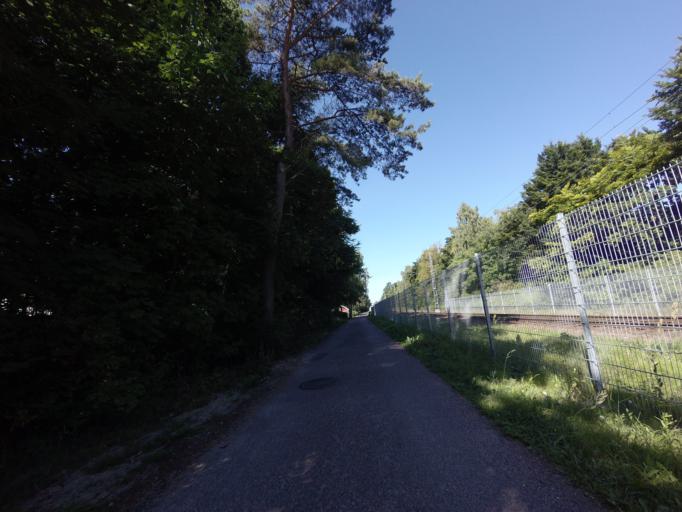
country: SE
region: Skane
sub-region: Ystads Kommun
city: Ystad
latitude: 55.4298
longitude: 13.8471
